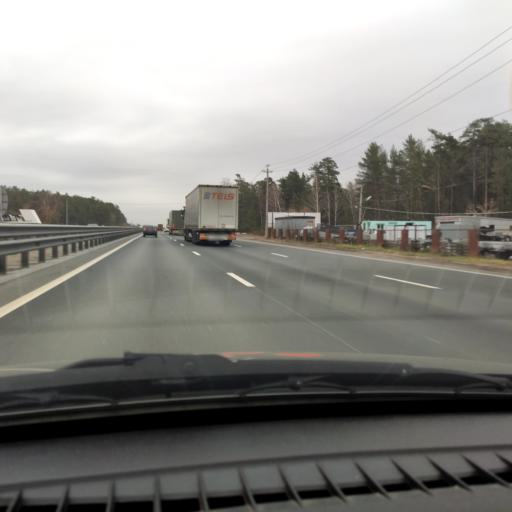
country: RU
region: Samara
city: Zhigulevsk
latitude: 53.5045
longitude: 49.5517
